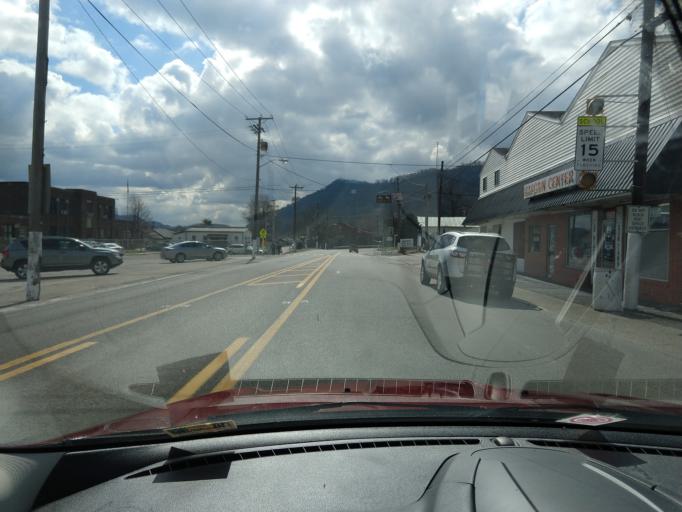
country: US
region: West Virginia
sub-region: Kanawha County
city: Marmet
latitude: 38.2462
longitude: -81.5677
